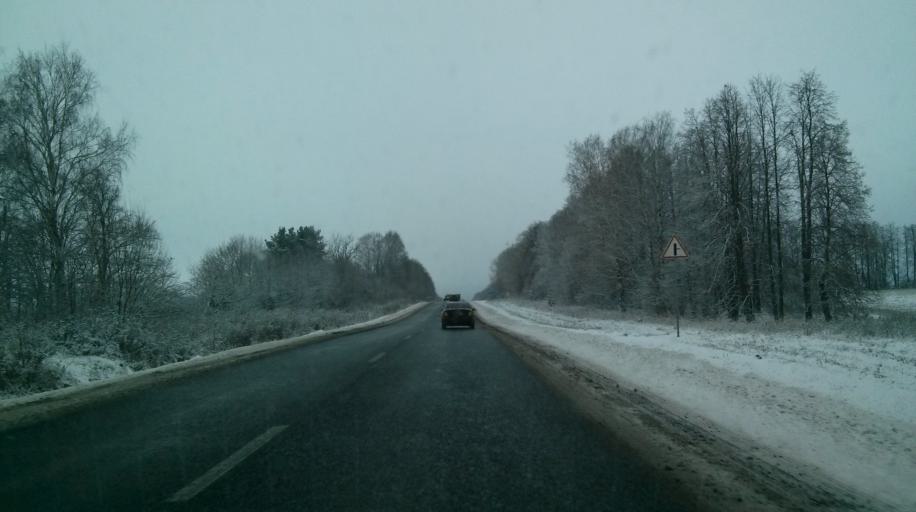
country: RU
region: Nizjnij Novgorod
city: Bogorodsk
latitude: 56.0601
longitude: 43.4180
